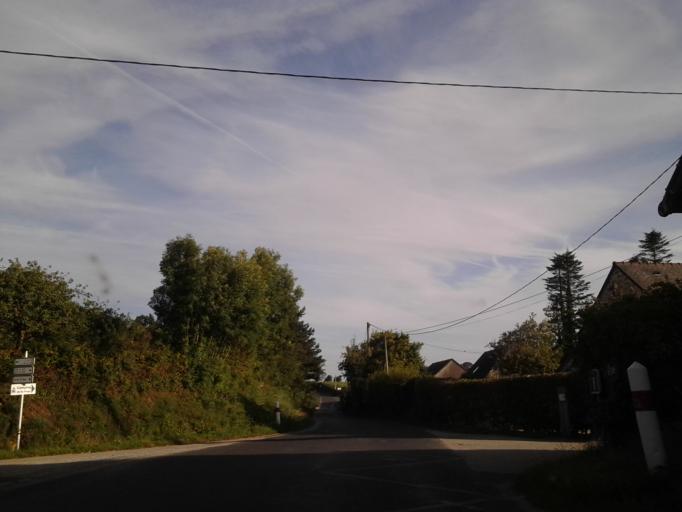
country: FR
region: Lower Normandy
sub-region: Departement de la Manche
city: Fermanville
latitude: 49.6543
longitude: -1.4483
